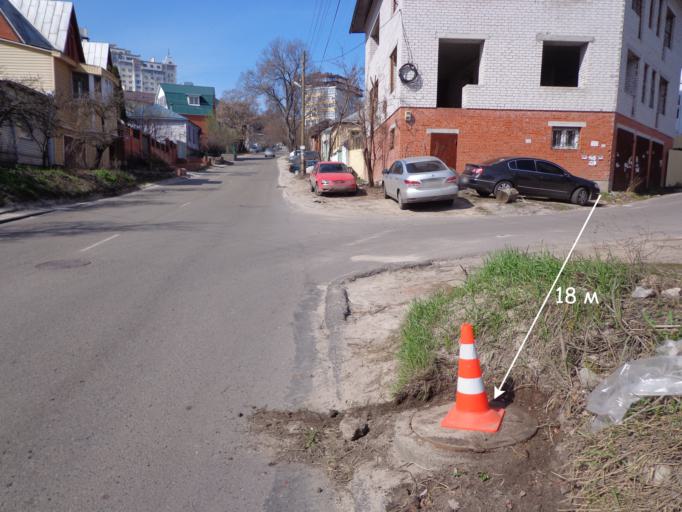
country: RU
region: Voronezj
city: Voronezh
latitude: 51.6613
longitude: 39.2136
